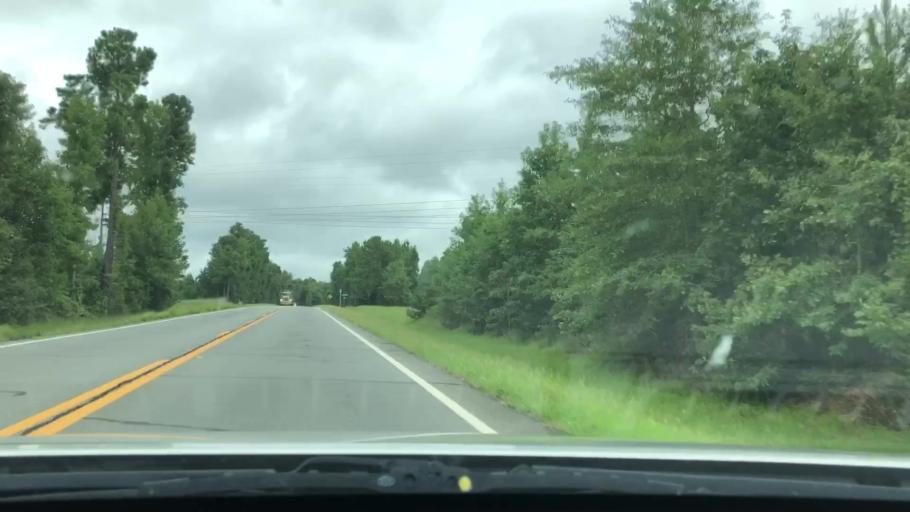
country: US
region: Georgia
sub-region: Pike County
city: Zebulon
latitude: 33.0442
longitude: -84.4900
